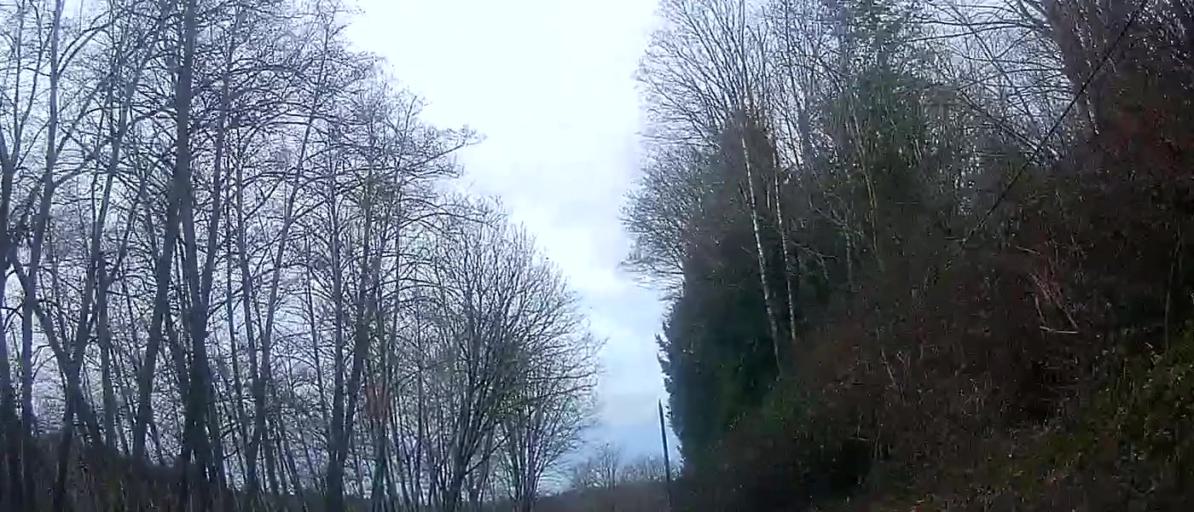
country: US
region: Washington
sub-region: Skagit County
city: Sedro-Woolley
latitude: 48.5548
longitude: -122.2931
